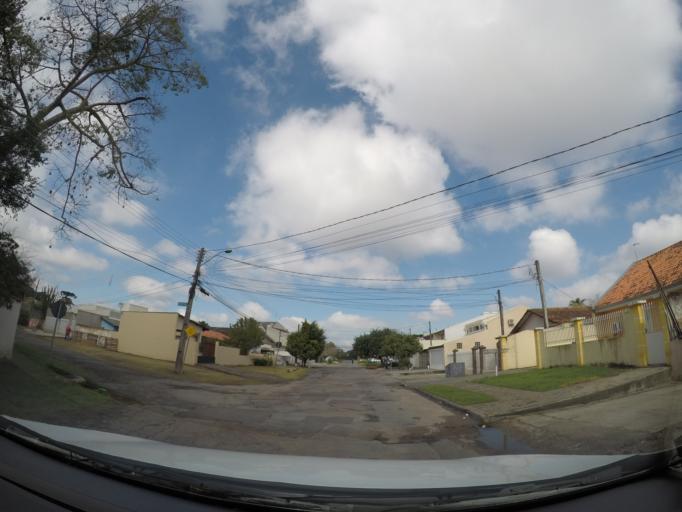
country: BR
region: Parana
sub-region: Sao Jose Dos Pinhais
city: Sao Jose dos Pinhais
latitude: -25.4897
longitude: -49.2202
